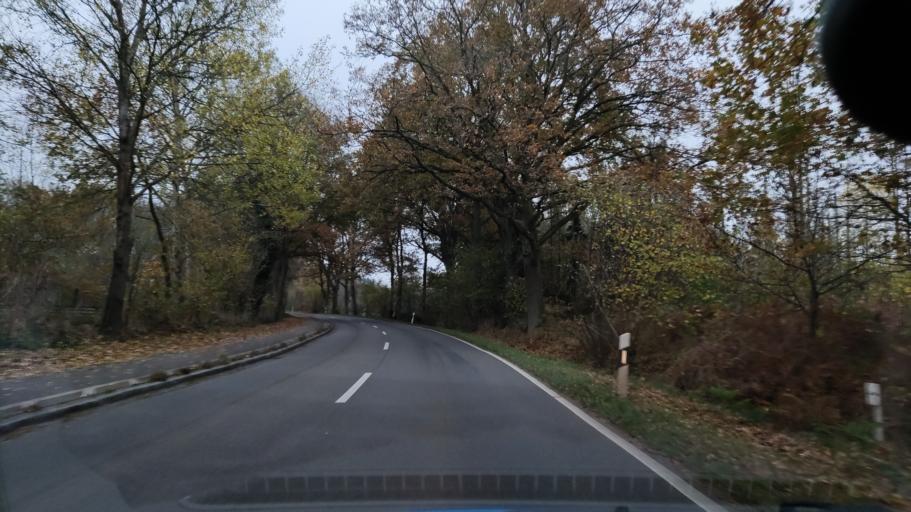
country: DE
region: Schleswig-Holstein
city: Gross Gronau
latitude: 53.8157
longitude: 10.7126
